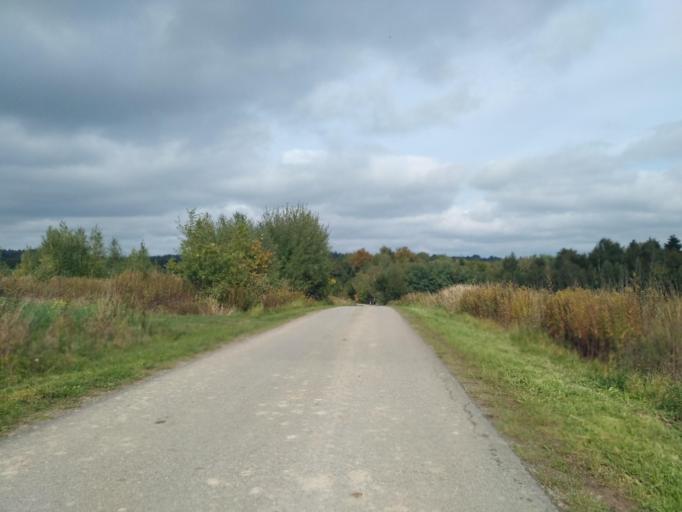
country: PL
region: Subcarpathian Voivodeship
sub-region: Powiat ropczycko-sedziszowski
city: Niedzwiada
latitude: 49.9332
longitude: 21.5037
